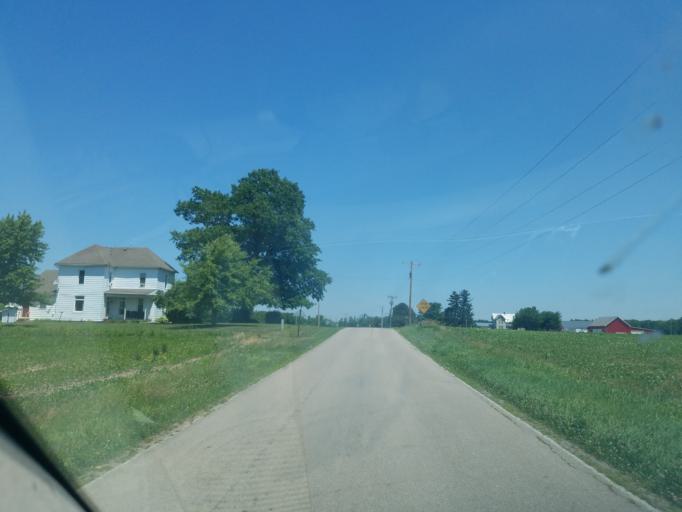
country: US
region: Ohio
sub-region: Mercer County
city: Rockford
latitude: 40.7403
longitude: -84.7370
